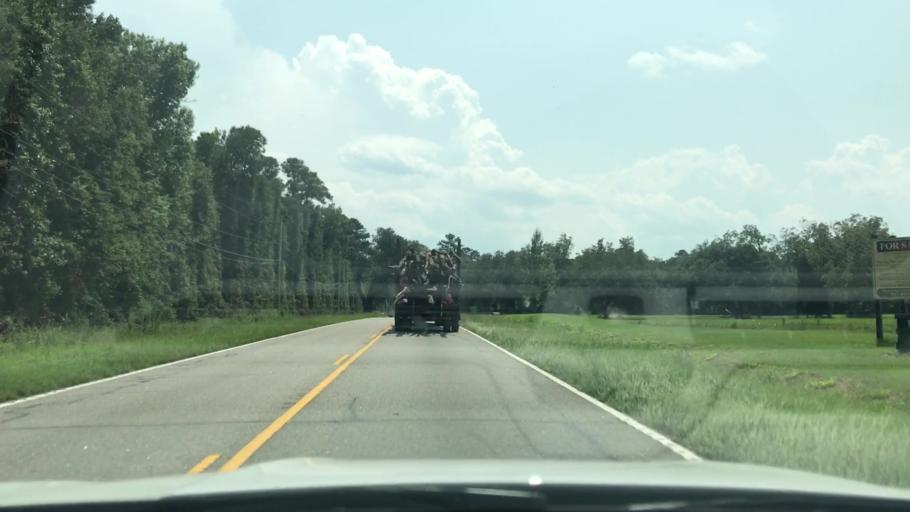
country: US
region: South Carolina
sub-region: Georgetown County
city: Georgetown
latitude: 33.4646
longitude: -79.2803
